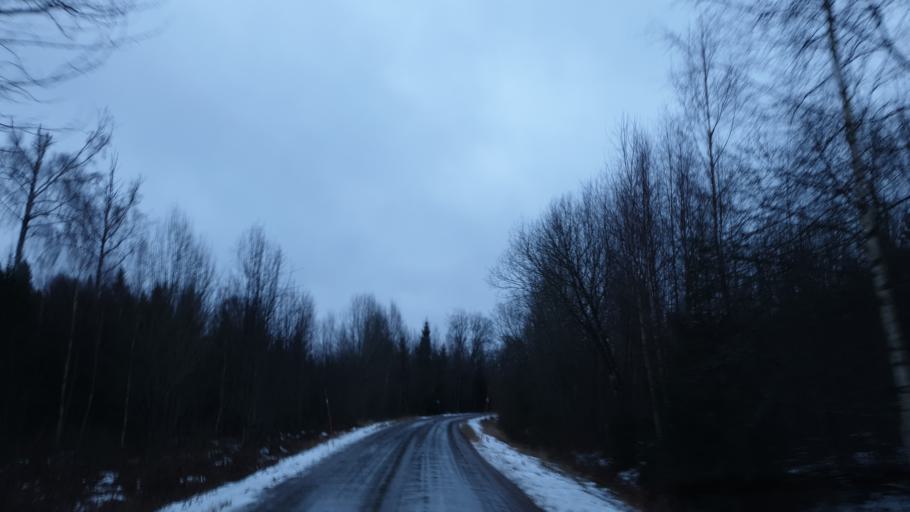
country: SE
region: Uppsala
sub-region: Tierps Kommun
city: Tierp
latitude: 60.3471
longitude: 17.4671
